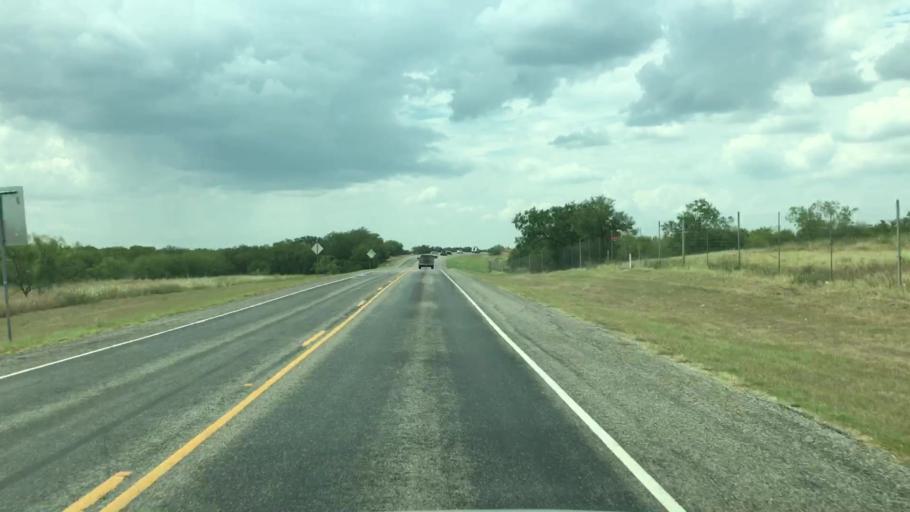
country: US
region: Texas
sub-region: Live Oak County
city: Three Rivers
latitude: 28.6395
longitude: -98.2802
